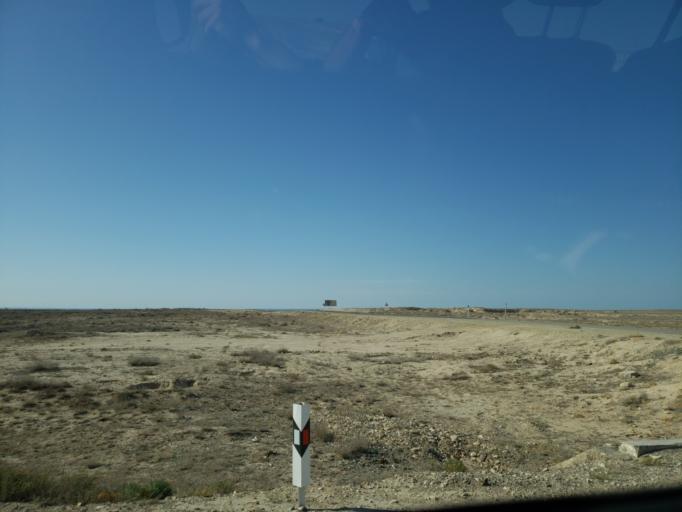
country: KZ
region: Mangghystau
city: Zhanaozen
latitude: 42.8251
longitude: 52.6354
